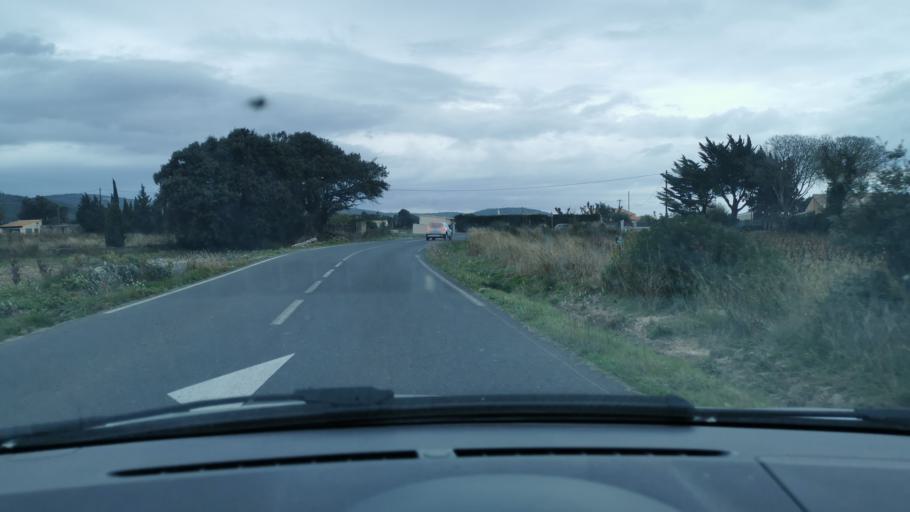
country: FR
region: Languedoc-Roussillon
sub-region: Departement de l'Herault
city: Balaruc-le-Vieux
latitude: 43.4411
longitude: 3.7134
